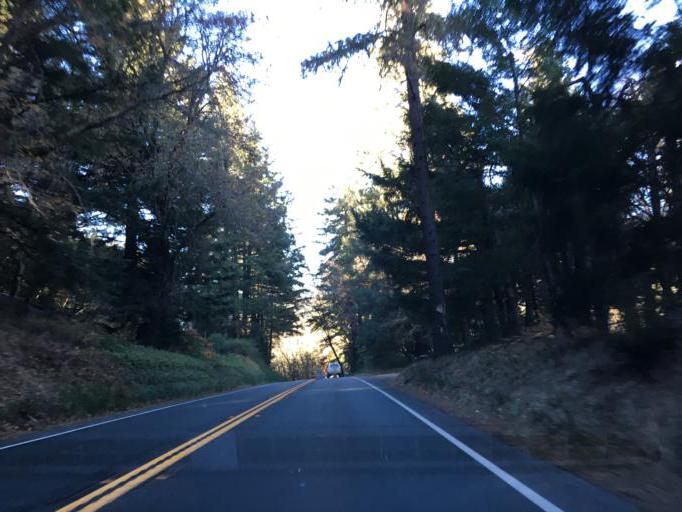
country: US
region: California
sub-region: Mendocino County
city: Brooktrails
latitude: 39.4908
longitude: -123.3632
